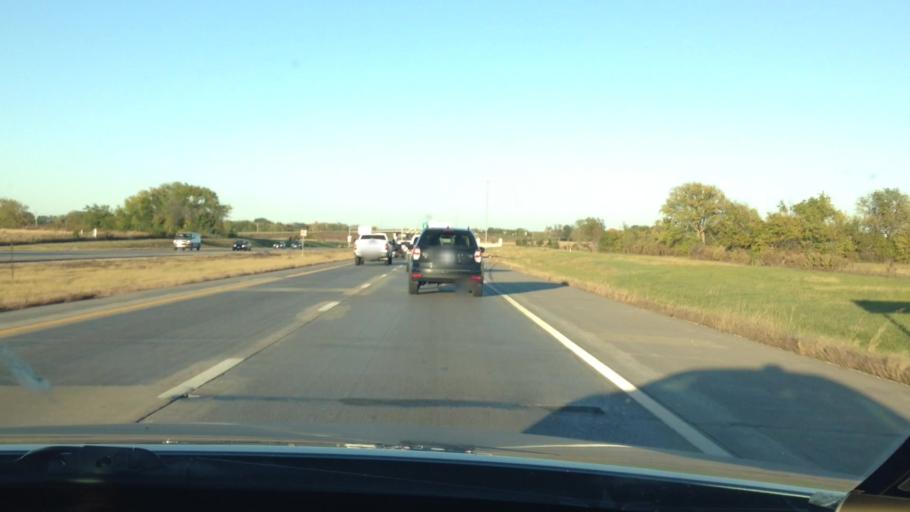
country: US
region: Kansas
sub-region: Johnson County
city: Olathe
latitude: 38.8356
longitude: -94.8486
